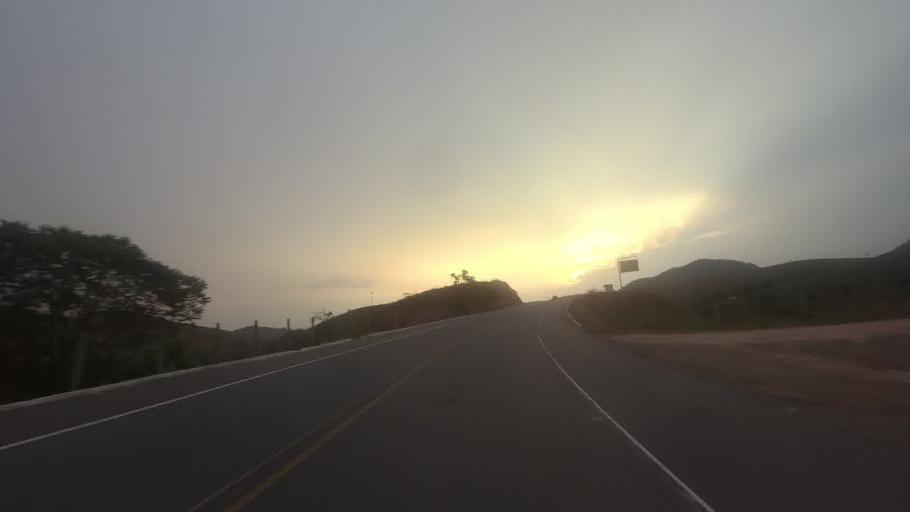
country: BR
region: Rio de Janeiro
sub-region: Carmo
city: Carmo
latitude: -21.7574
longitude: -42.4833
